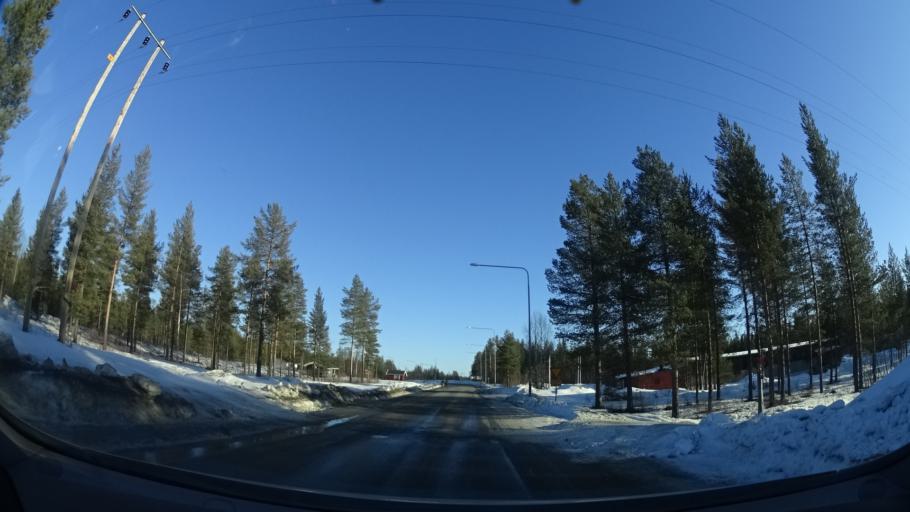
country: SE
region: Vaesterbotten
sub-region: Skelleftea Kommun
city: Langsele
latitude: 65.0544
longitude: 20.0544
